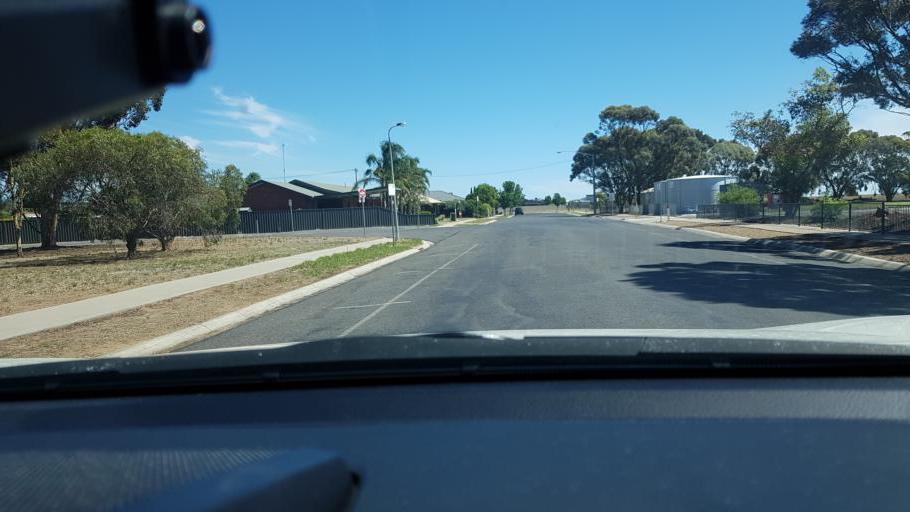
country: AU
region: Victoria
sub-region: Horsham
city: Horsham
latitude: -36.7118
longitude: 142.1839
